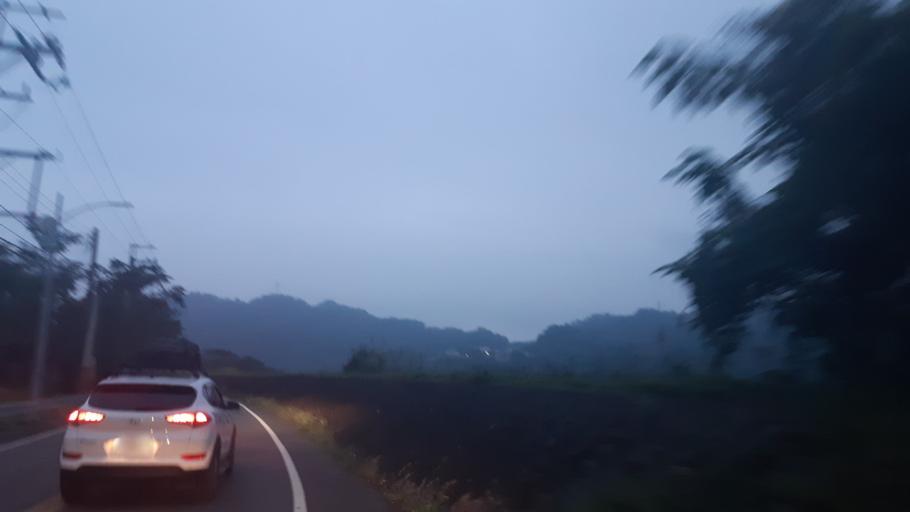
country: TW
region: Taiwan
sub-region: Hsinchu
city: Zhubei
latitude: 24.7101
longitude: 121.1677
